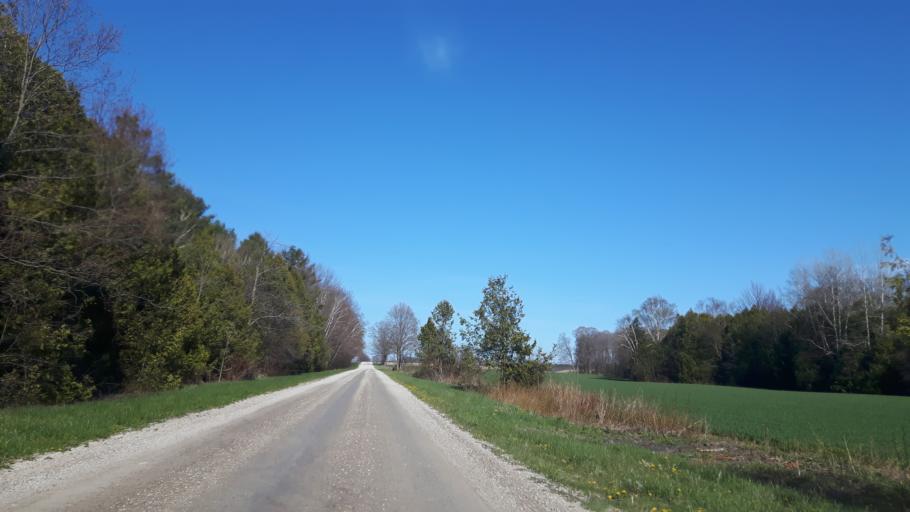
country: CA
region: Ontario
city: Goderich
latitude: 43.6612
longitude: -81.6998
